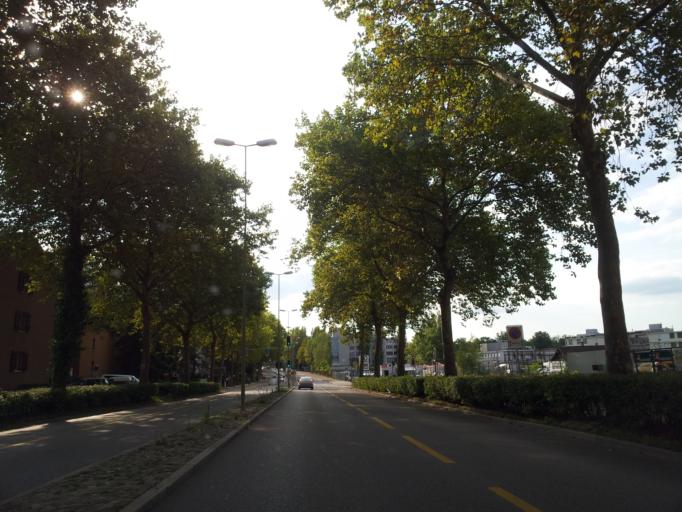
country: CH
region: Zurich
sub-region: Bezirk Dietikon
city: Schlieren / Spital
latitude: 47.3970
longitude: 8.4349
